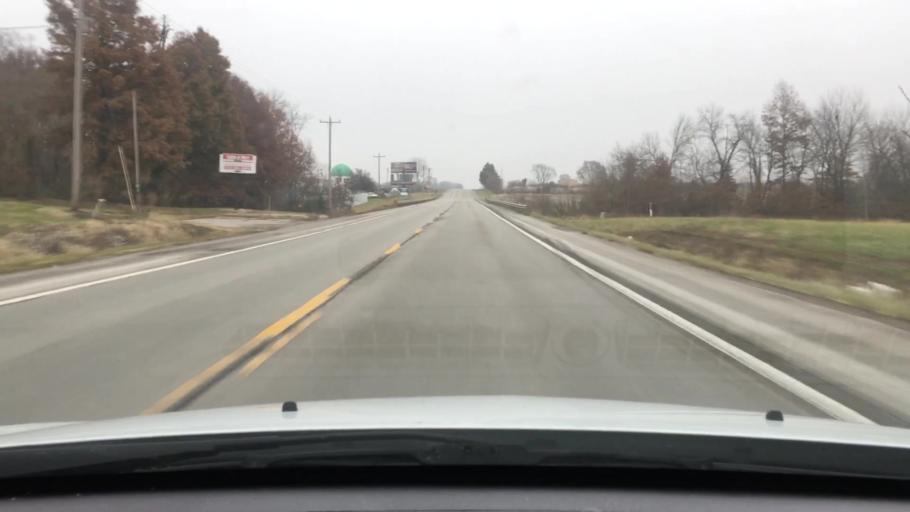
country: US
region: Missouri
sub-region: Audrain County
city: Mexico
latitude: 39.1638
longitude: -91.8085
